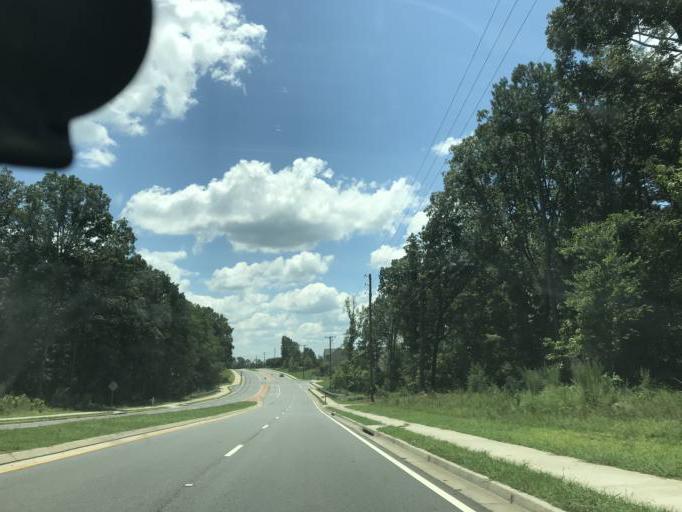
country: US
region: Georgia
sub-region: Fulton County
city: Milton
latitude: 34.1559
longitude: -84.2350
